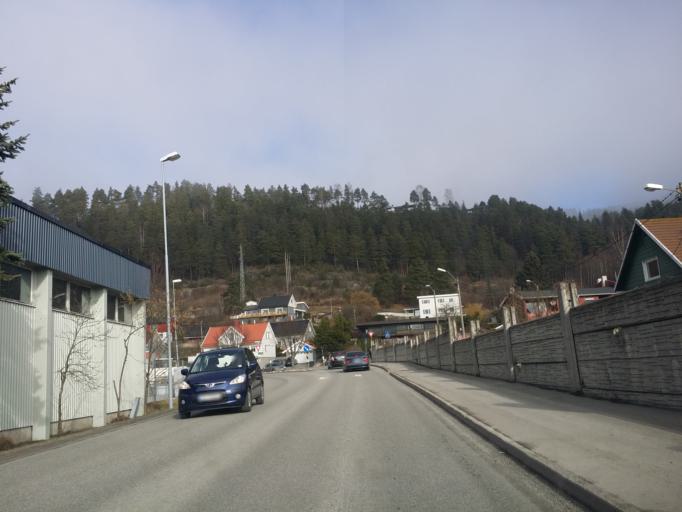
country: NO
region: Buskerud
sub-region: Nedre Eiker
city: Mjondalen
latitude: 59.7567
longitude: 10.0295
